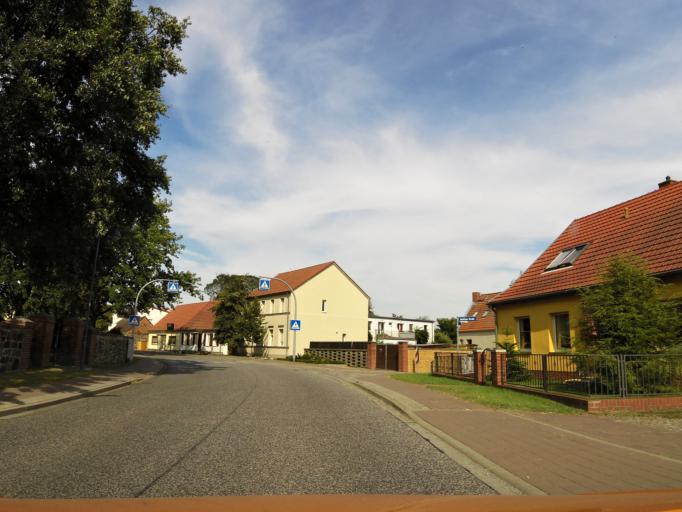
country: DE
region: Brandenburg
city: Michendorf
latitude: 52.3170
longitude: 13.1272
